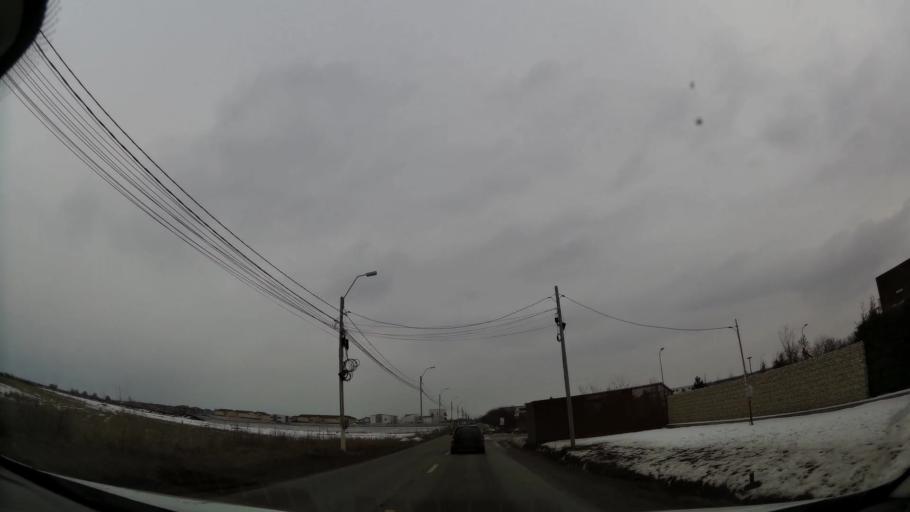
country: RO
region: Ilfov
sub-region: Comuna Tunari
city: Tunari
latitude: 44.5507
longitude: 26.1162
